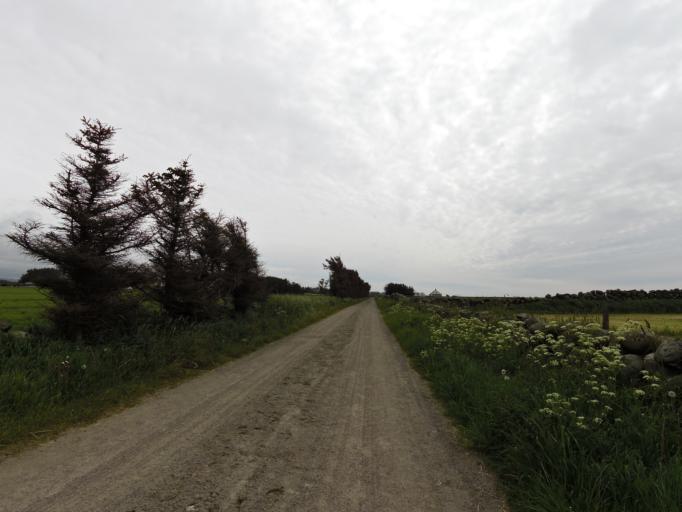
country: NO
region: Rogaland
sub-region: Ha
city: Naerbo
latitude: 58.6741
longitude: 5.5486
